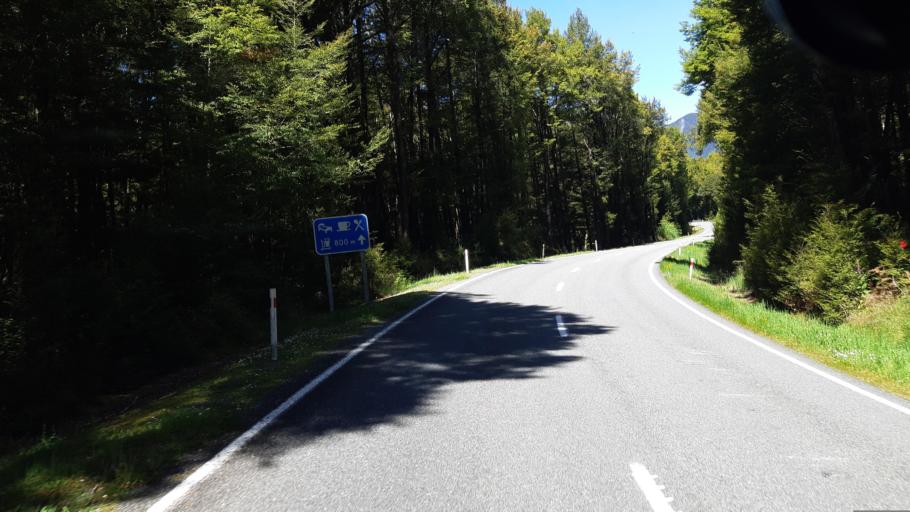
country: NZ
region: West Coast
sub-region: Buller District
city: Westport
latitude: -42.3323
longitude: 172.1726
